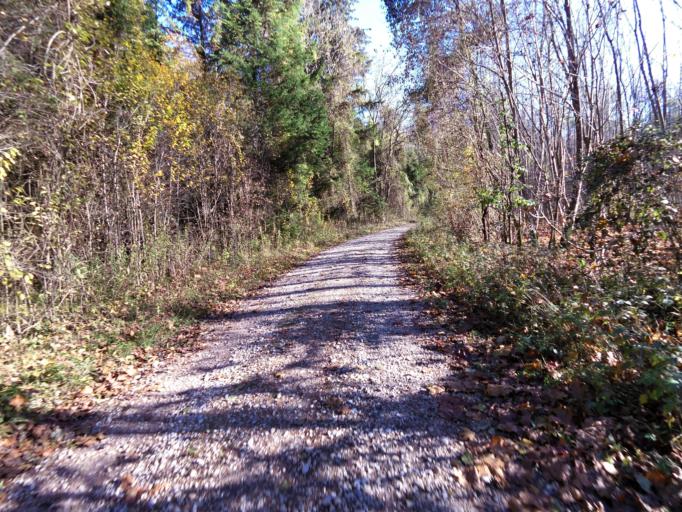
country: DE
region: Bavaria
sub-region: Upper Bavaria
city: Wang
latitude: 48.5040
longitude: 11.9801
